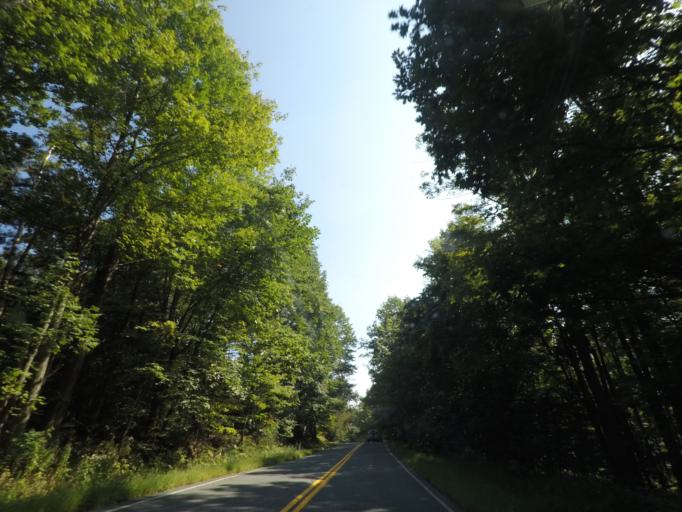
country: US
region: New York
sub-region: Rensselaer County
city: Poestenkill
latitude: 42.7206
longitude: -73.5096
